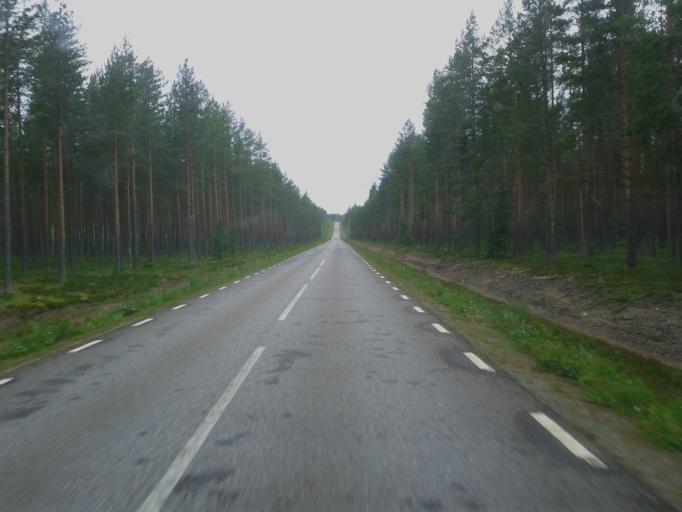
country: SE
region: Vaesterbotten
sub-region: Skelleftea Kommun
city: Kage
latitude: 64.9187
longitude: 20.9312
